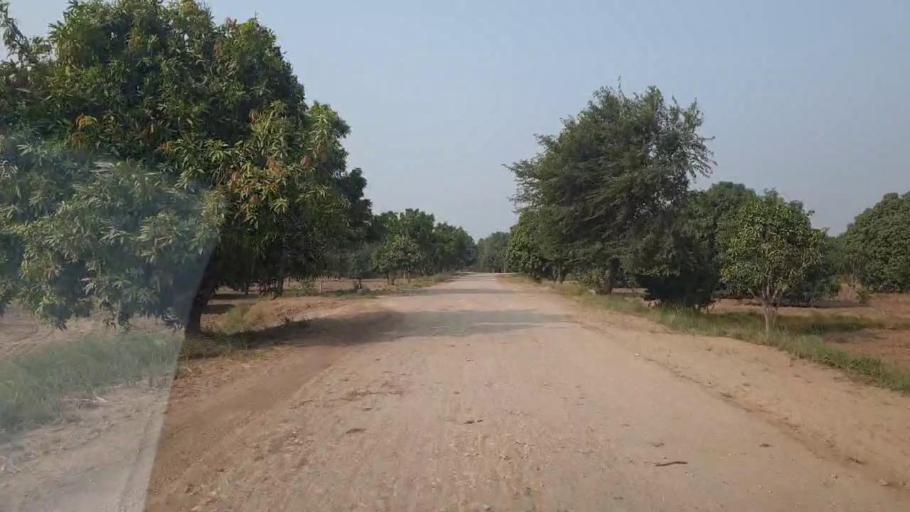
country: PK
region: Sindh
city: Tando Jam
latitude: 25.3307
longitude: 68.5193
